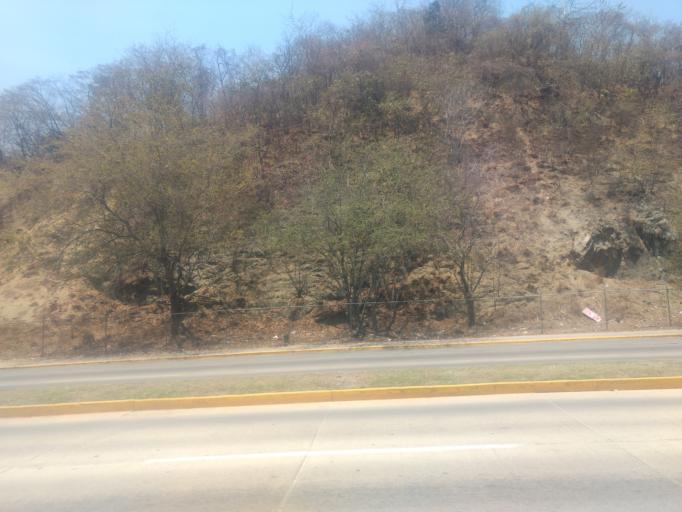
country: MX
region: Colima
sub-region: Manzanillo
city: Manzanillo
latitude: 19.1155
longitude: -104.3484
